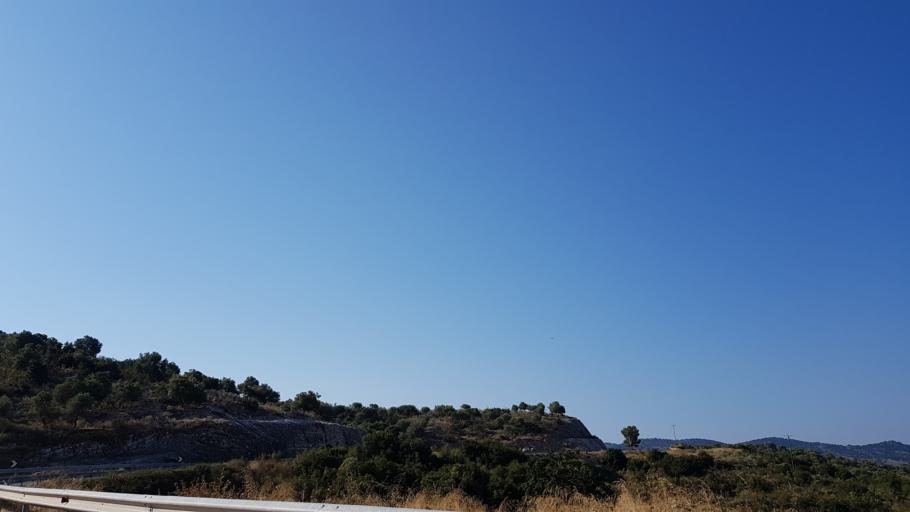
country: AL
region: Vlore
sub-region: Rrethi i Sarandes
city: Xarre
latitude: 39.7513
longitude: 20.0044
